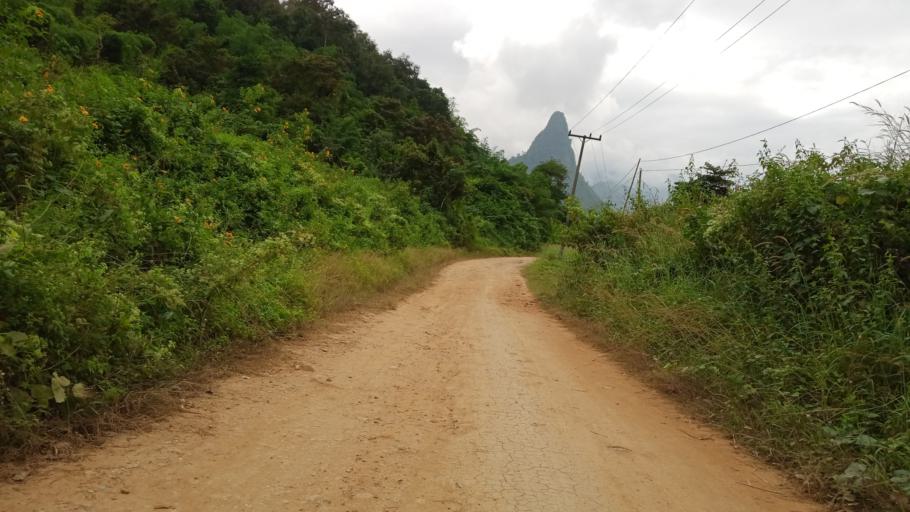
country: LA
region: Xiangkhoang
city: Phonsavan
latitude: 19.0860
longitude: 103.0097
